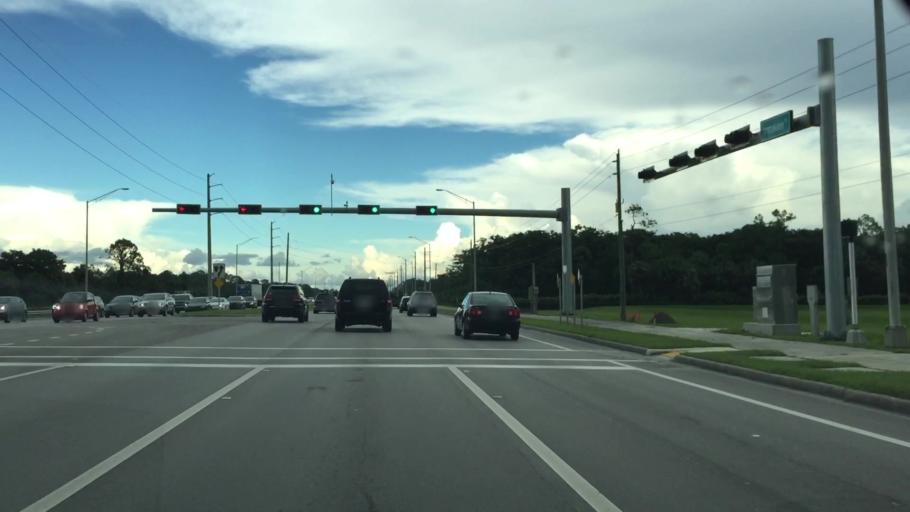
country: US
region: Florida
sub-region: Collier County
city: Orangetree
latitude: 26.2753
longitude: -81.6242
